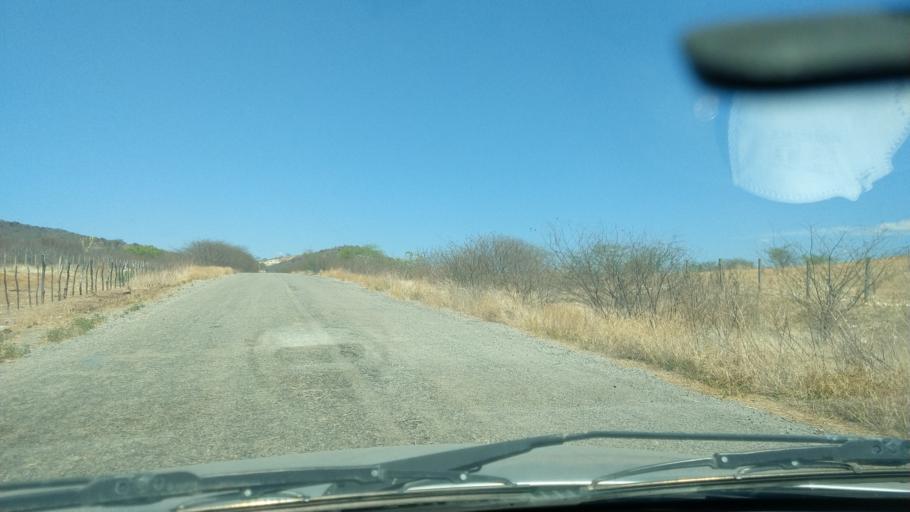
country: BR
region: Rio Grande do Norte
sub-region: Sao Tome
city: Sao Tome
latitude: -5.9741
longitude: -36.1511
